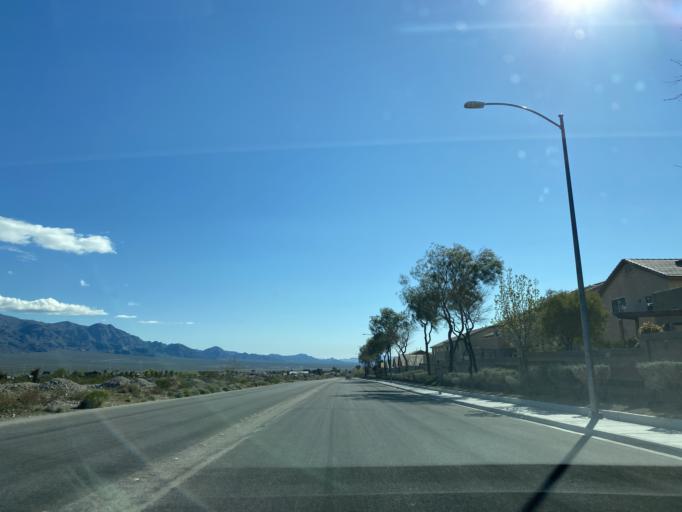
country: US
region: Nevada
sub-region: Clark County
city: Summerlin South
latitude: 36.3287
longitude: -115.2949
